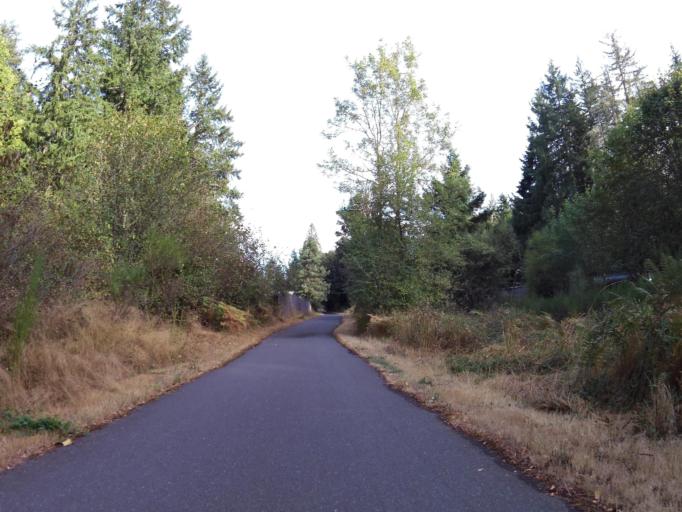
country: US
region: Washington
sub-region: Thurston County
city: Tenino
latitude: 46.9211
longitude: -122.8040
